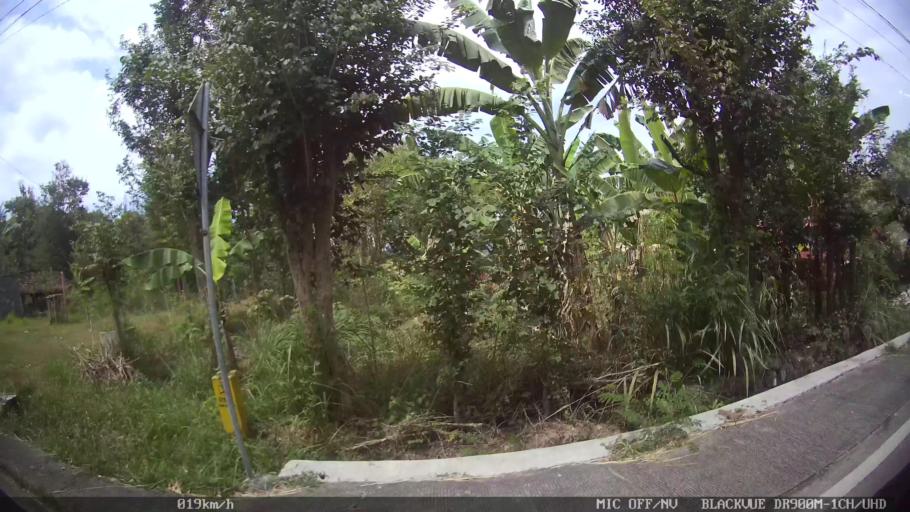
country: ID
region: Central Java
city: Candi Prambanan
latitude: -7.7837
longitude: 110.5086
